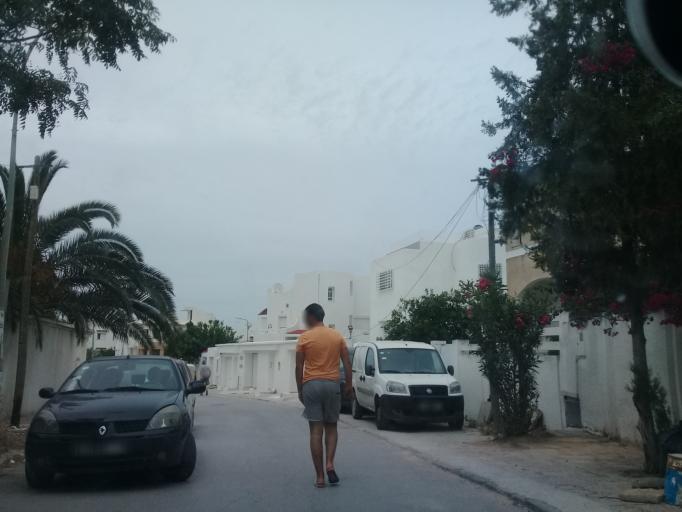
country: TN
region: Tunis
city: Tunis
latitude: 36.8436
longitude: 10.1557
